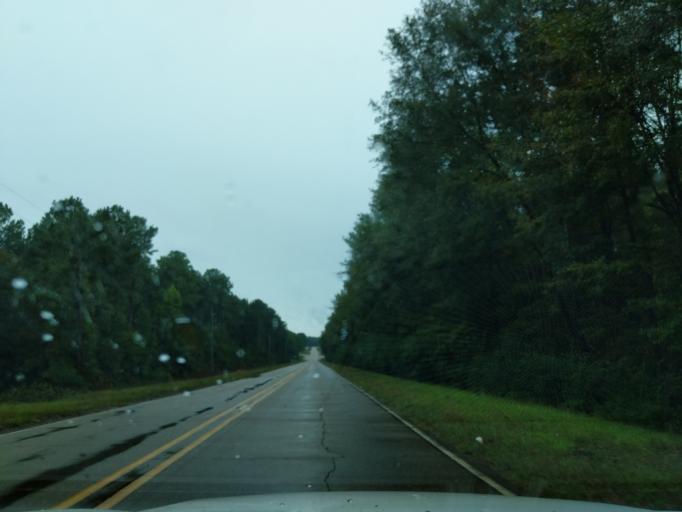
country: US
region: Louisiana
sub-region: Bienville Parish
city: Arcadia
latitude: 32.5559
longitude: -93.0541
